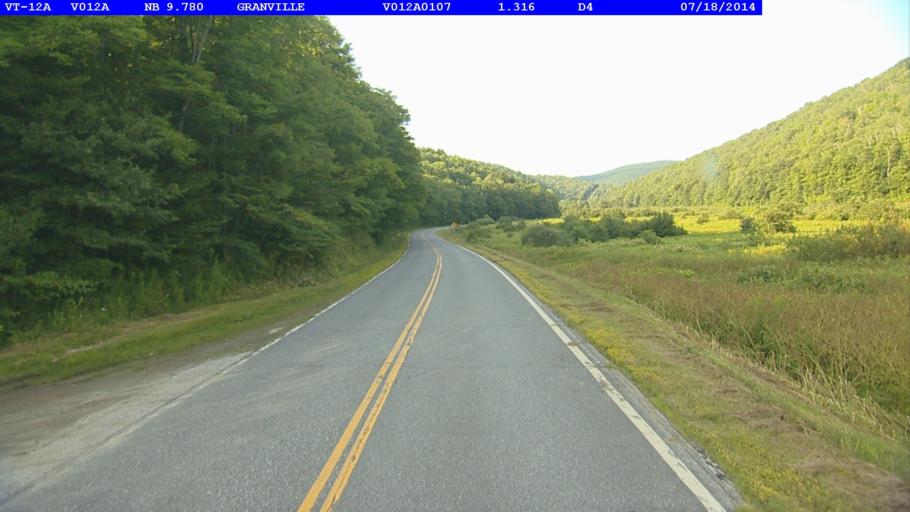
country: US
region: Vermont
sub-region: Orange County
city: Randolph
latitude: 44.0289
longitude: -72.7590
